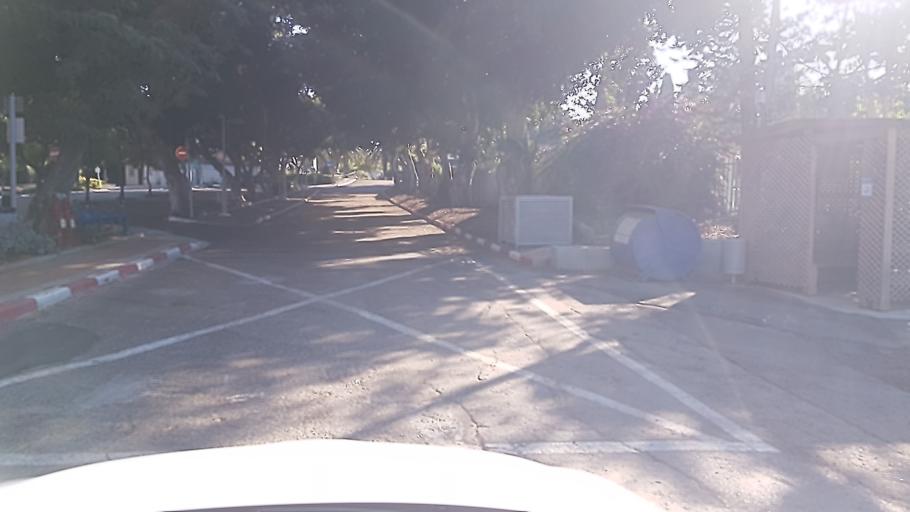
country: IL
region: Central District
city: Kfar Saba
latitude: 32.2024
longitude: 34.9280
